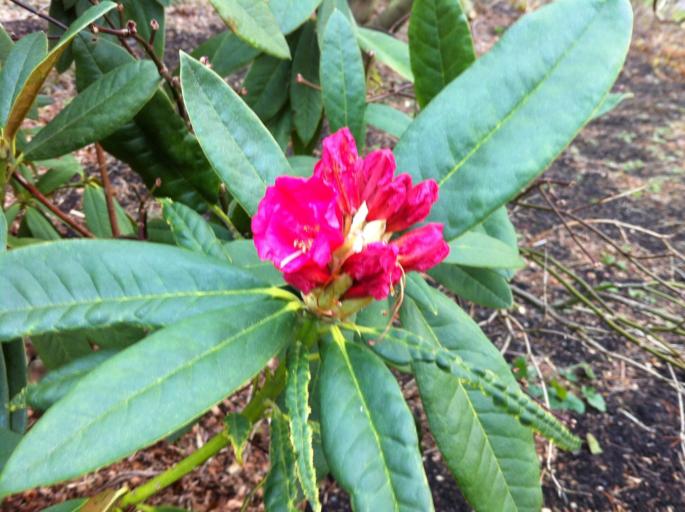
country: GB
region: Scotland
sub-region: Edinburgh
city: Edinburgh
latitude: 55.9651
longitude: -3.2114
